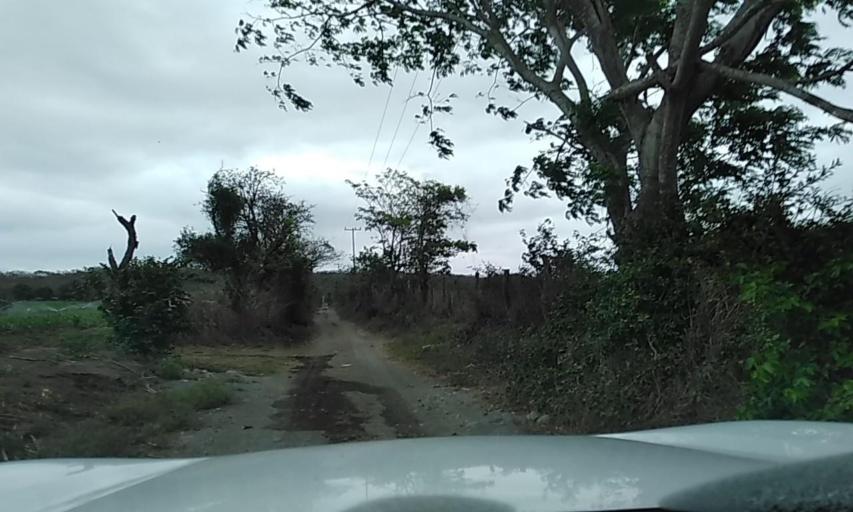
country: MX
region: Veracruz
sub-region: Paso de Ovejas
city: El Hatito
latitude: 19.2754
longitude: -96.3151
